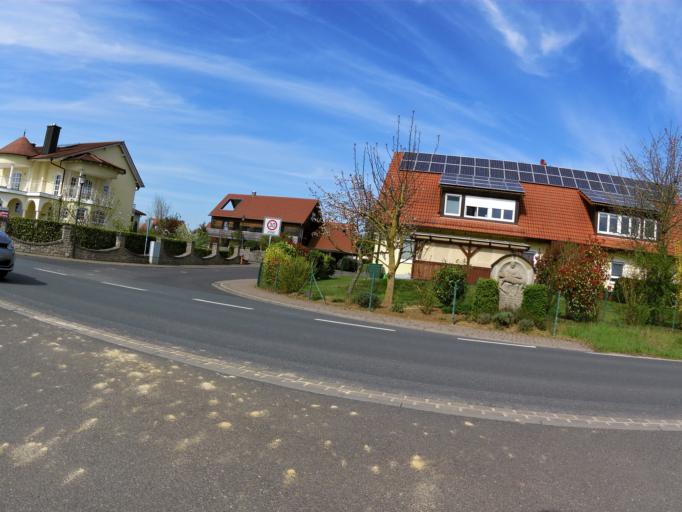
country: DE
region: Bavaria
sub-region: Regierungsbezirk Unterfranken
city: Unterpleichfeld
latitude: 49.8706
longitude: 10.0364
